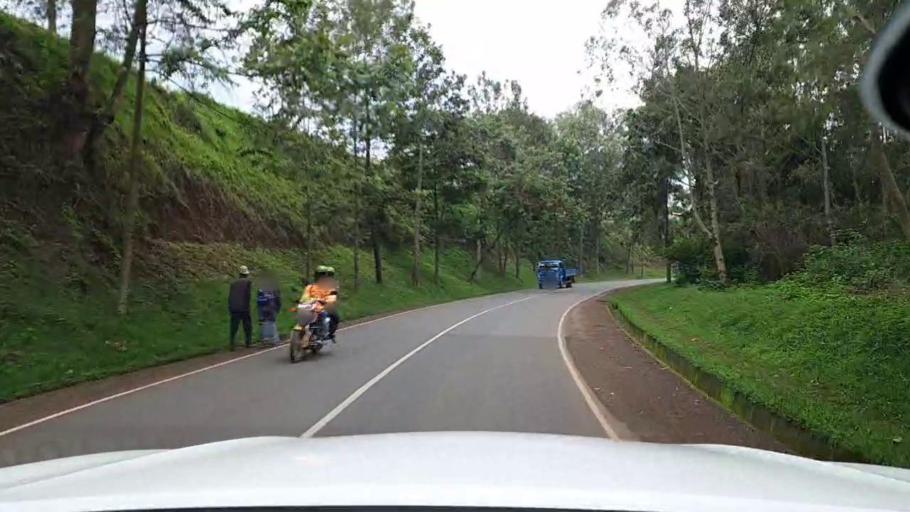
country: RW
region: Western Province
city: Cyangugu
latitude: -2.5390
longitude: 28.8992
